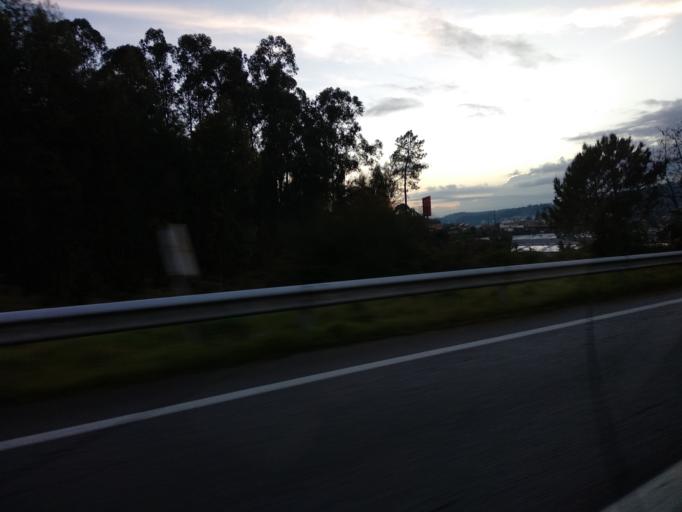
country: PT
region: Braga
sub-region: Braga
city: Oliveira
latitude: 41.4953
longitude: -8.4668
